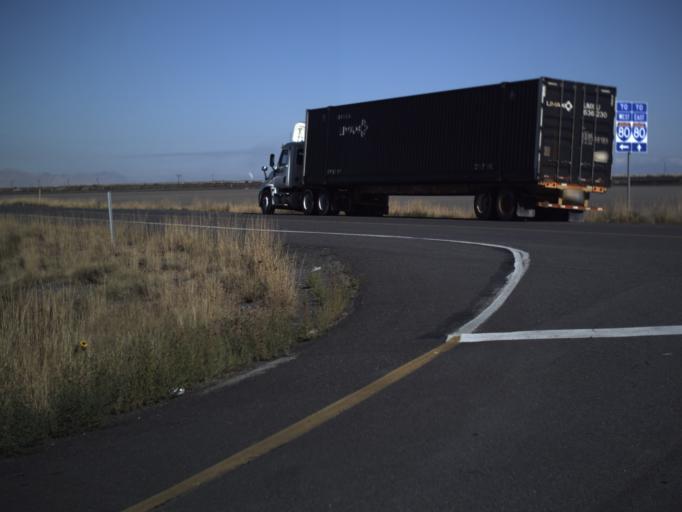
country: US
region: Utah
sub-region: Tooele County
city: Grantsville
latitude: 40.7088
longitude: -112.5223
